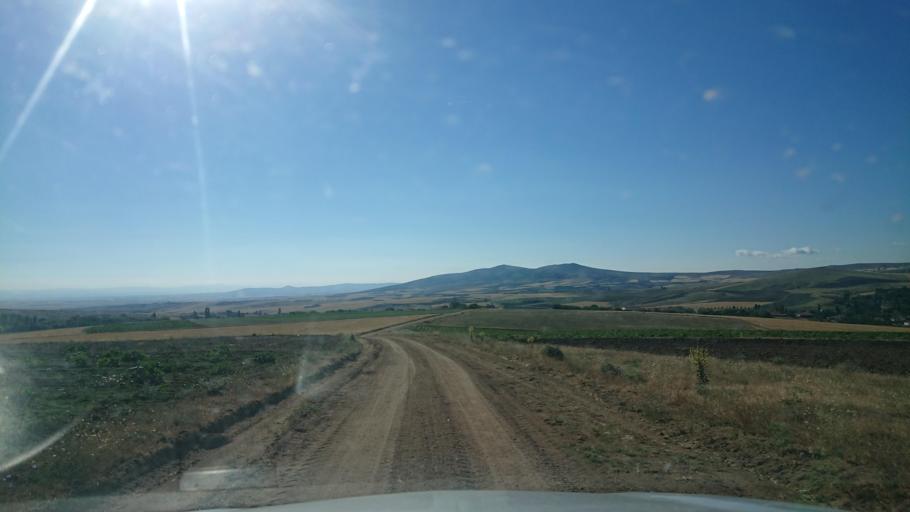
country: TR
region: Aksaray
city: Agacoren
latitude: 38.8291
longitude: 33.9494
